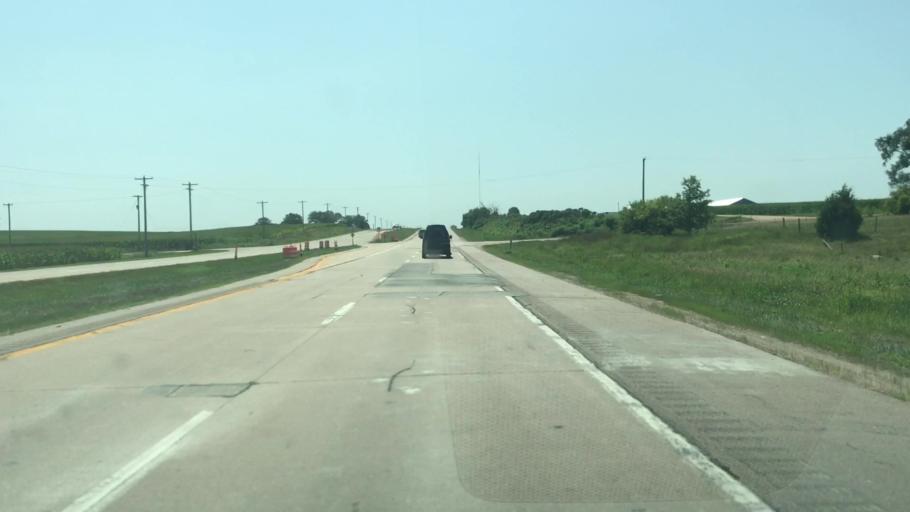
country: US
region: Nebraska
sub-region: Adams County
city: Hastings
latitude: 40.6709
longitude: -98.3823
